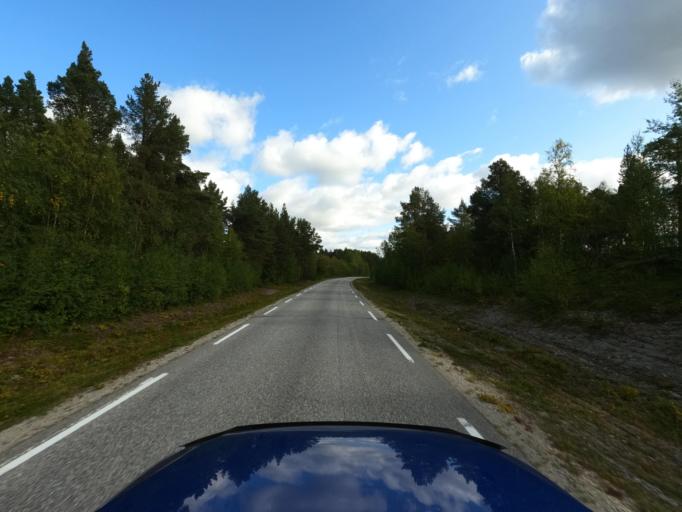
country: NO
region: Finnmark Fylke
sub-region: Karasjok
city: Karasjohka
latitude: 69.4323
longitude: 25.1359
